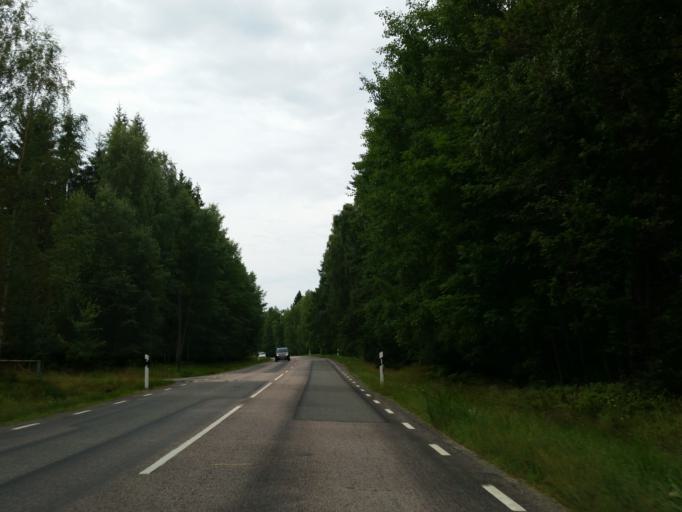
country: SE
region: Stockholm
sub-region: Nykvarns Kommun
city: Nykvarn
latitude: 59.1932
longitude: 17.5269
